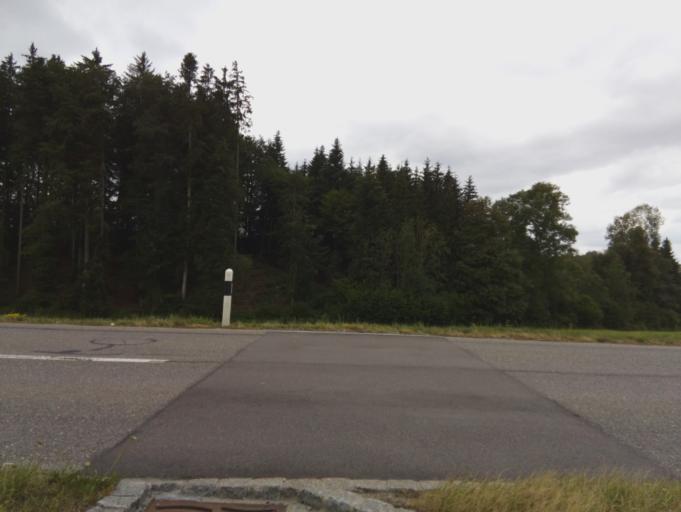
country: CH
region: Saint Gallen
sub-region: Wahlkreis Toggenburg
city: Lutisburg
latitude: 47.4016
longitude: 9.0812
